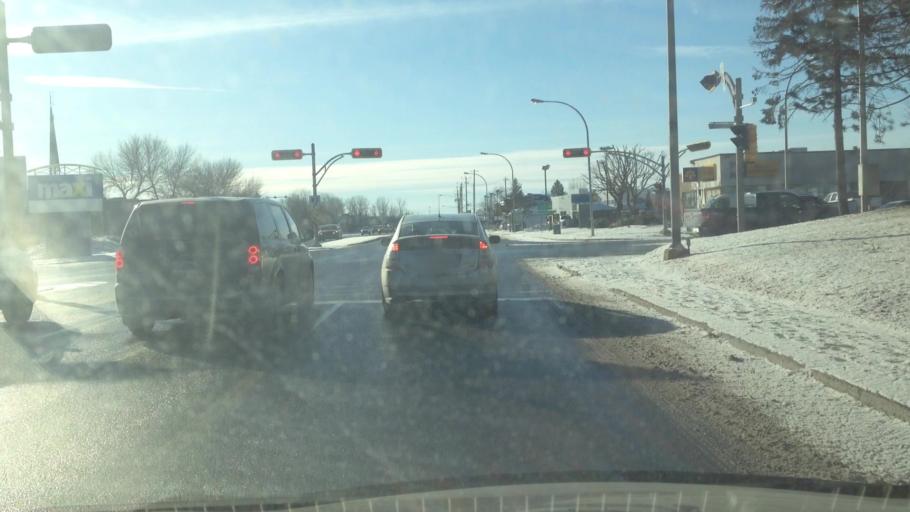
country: CA
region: Quebec
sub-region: Monteregie
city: Chateauguay
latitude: 45.3589
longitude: -73.7159
